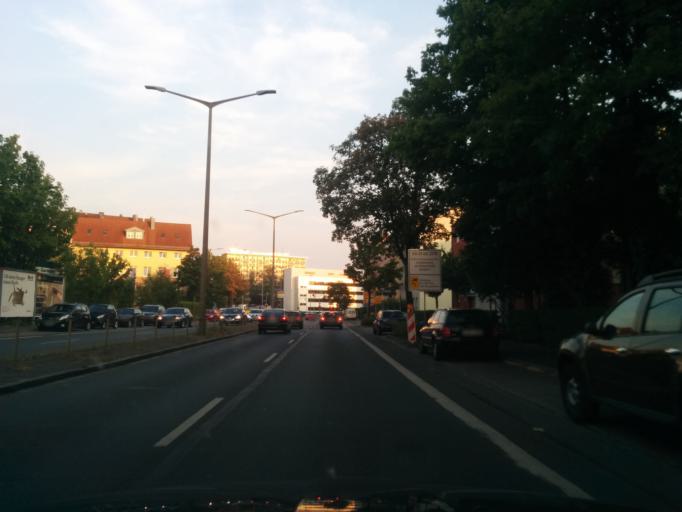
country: DE
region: Bavaria
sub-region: Regierungsbezirk Mittelfranken
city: Nuernberg
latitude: 49.4682
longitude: 11.0965
